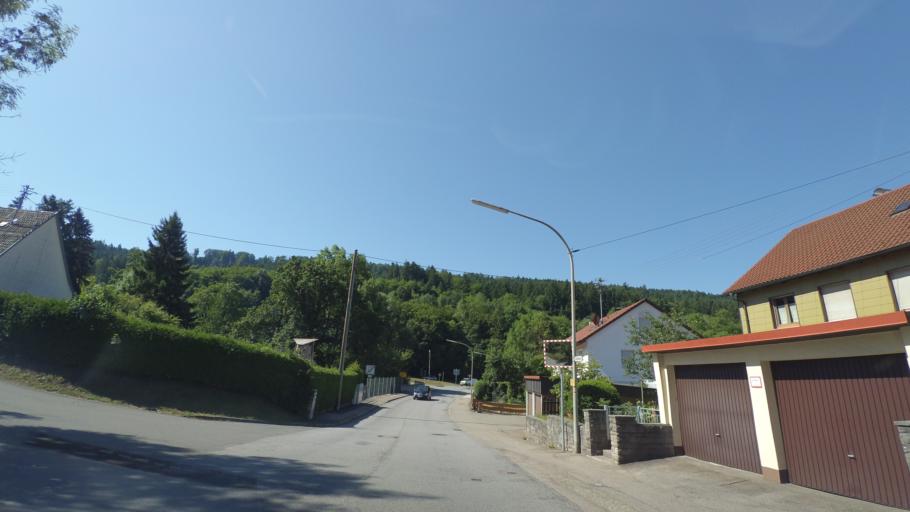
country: DE
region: Baden-Wuerttemberg
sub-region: Regierungsbezirk Stuttgart
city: Murrhardt
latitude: 48.9753
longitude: 9.6038
